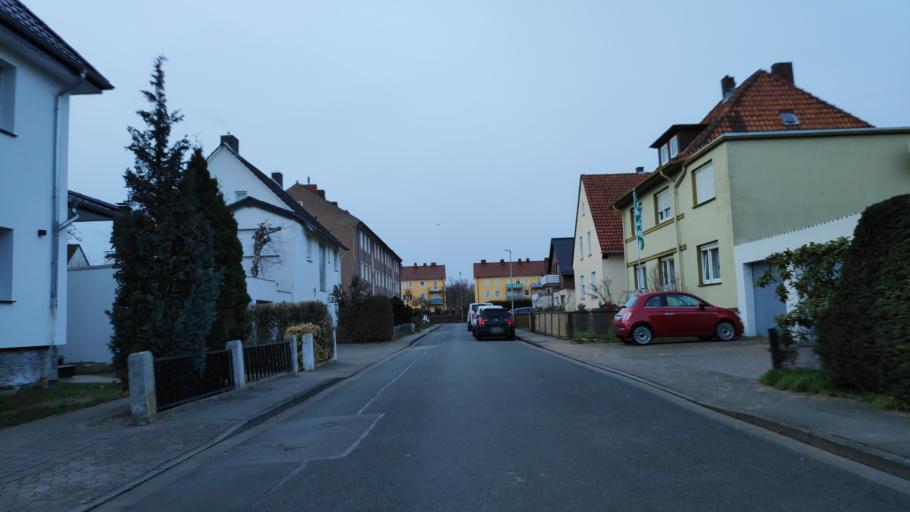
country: DE
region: North Rhine-Westphalia
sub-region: Regierungsbezirk Detmold
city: Minden
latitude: 52.2935
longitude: 8.9446
